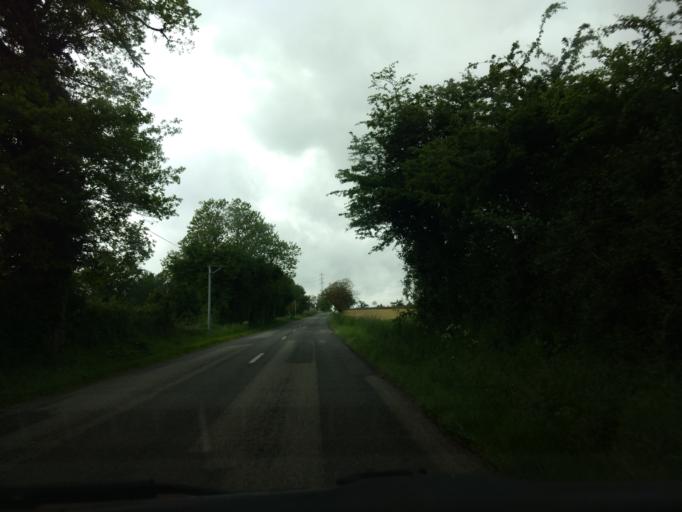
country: FR
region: Midi-Pyrenees
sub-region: Departement de l'Aveyron
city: Montbazens
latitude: 44.5002
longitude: 2.1996
